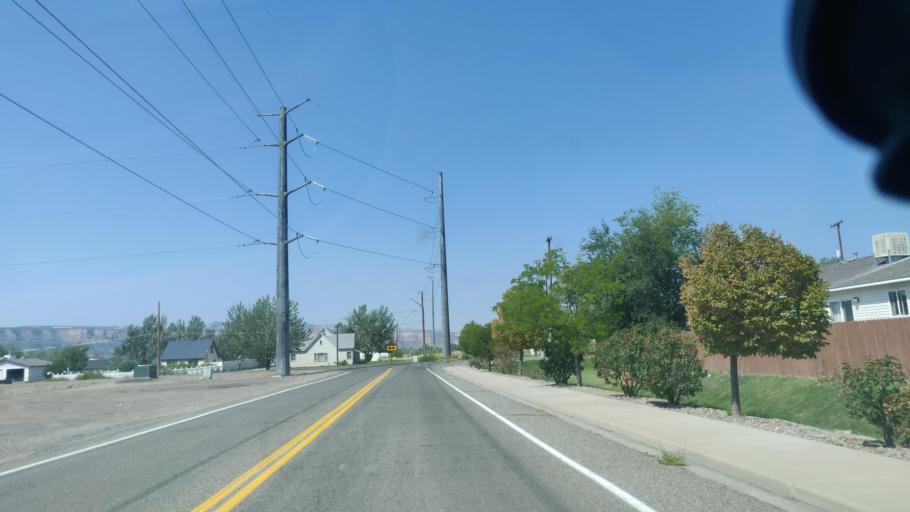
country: US
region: Colorado
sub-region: Mesa County
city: Redlands
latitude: 39.0991
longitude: -108.5884
